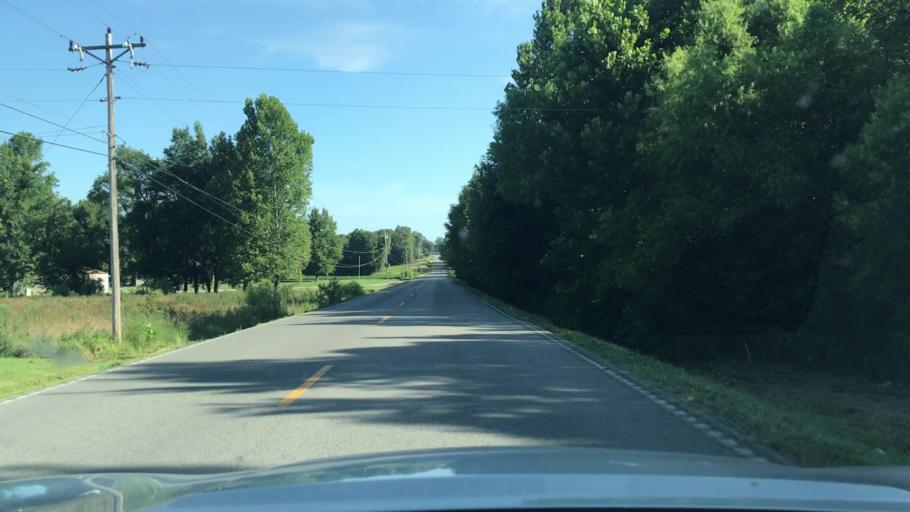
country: US
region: Kentucky
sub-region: Muhlenberg County
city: Greenville
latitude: 37.1502
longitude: -87.1414
